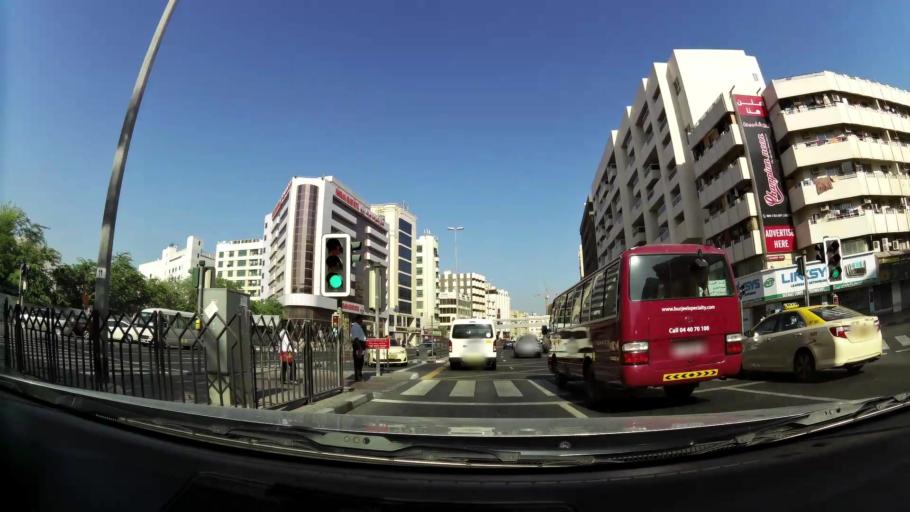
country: AE
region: Ash Shariqah
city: Sharjah
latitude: 25.2594
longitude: 55.2898
